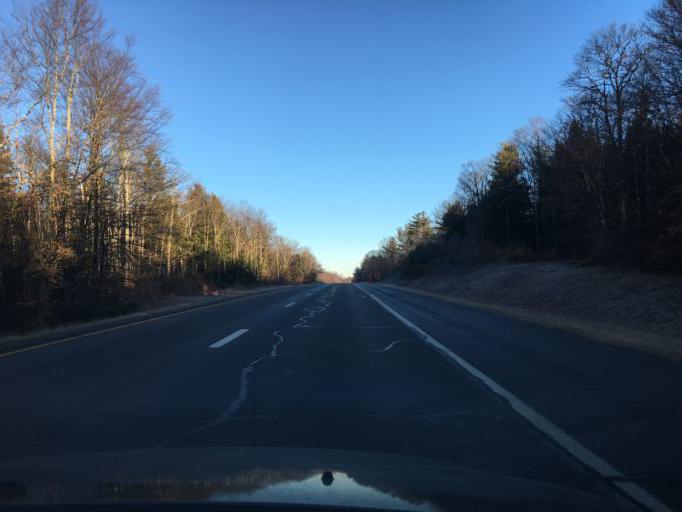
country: US
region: New Hampshire
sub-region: Belknap County
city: Sanbornton
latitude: 43.5433
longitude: -71.6153
